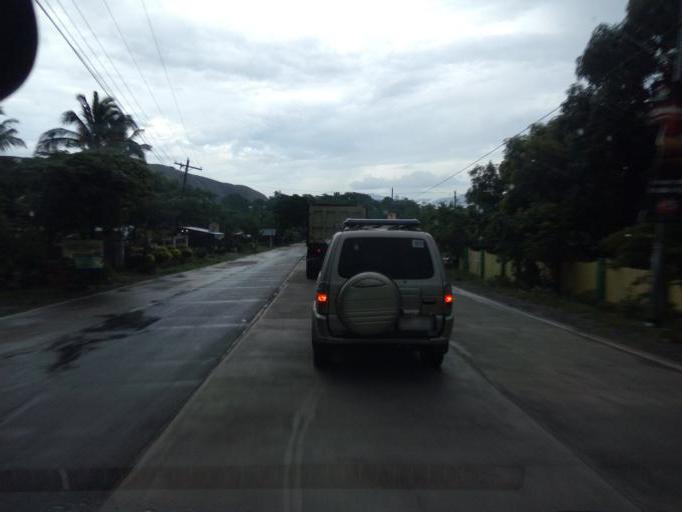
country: PH
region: Cagayan Valley
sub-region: Province of Nueva Vizcaya
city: Banganan
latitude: 16.3152
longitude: 121.0522
